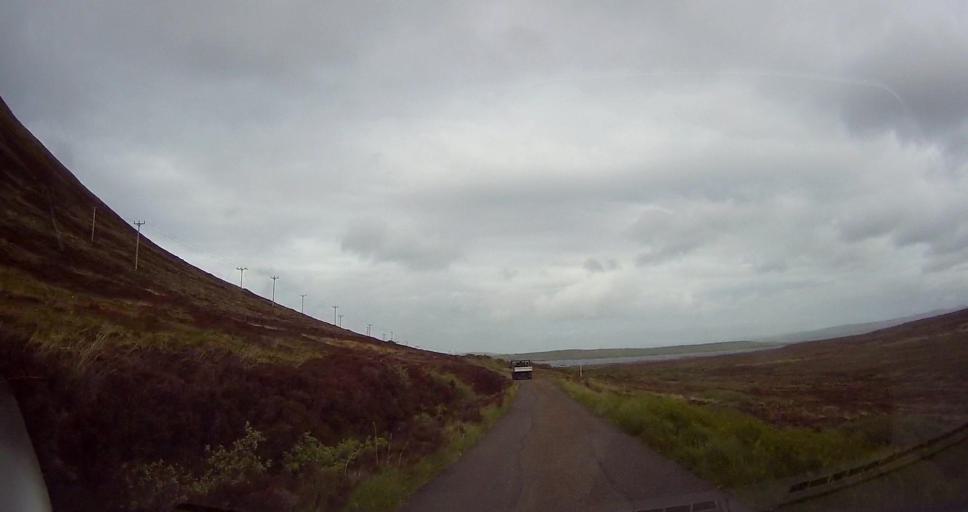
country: GB
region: Scotland
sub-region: Orkney Islands
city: Stromness
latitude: 58.8916
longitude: -3.3146
